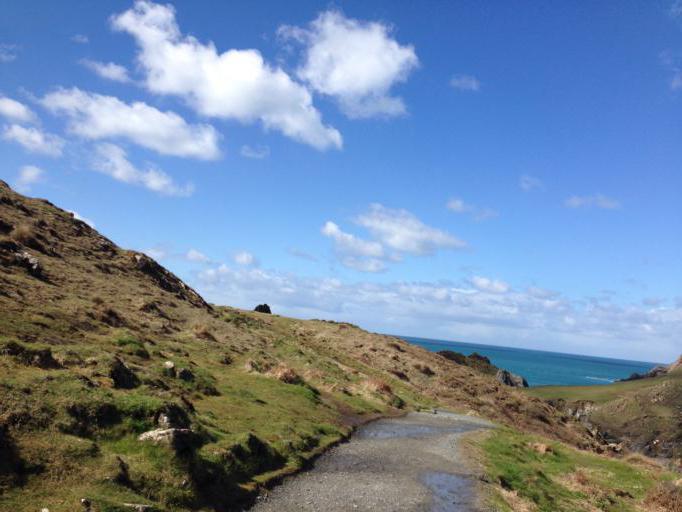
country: GB
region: England
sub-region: Cornwall
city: Landewednack
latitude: 49.9751
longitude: -5.2278
